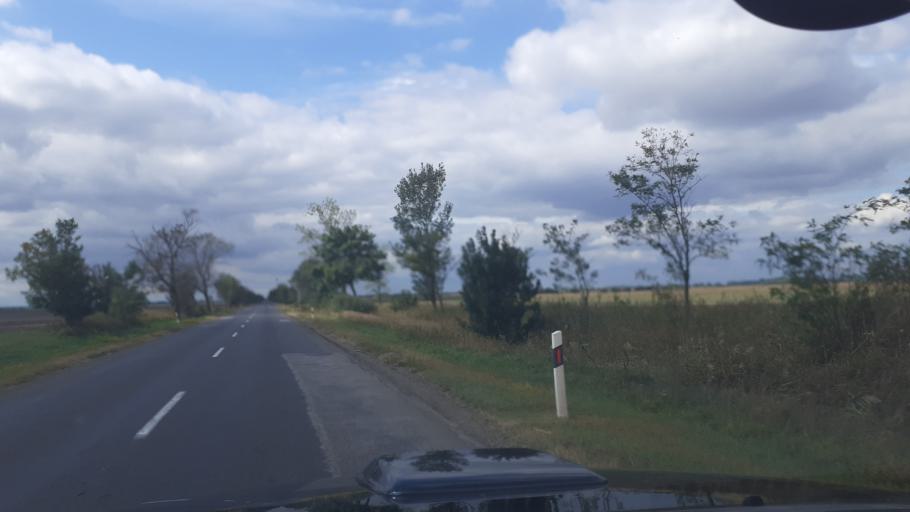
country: HU
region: Bacs-Kiskun
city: Solt
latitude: 46.7981
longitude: 19.0840
